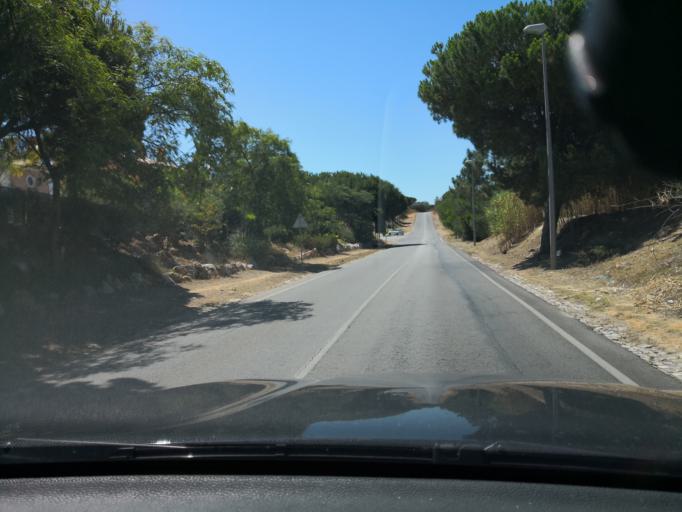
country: PT
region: Faro
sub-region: Loule
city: Vilamoura
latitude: 37.0918
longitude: -8.1027
